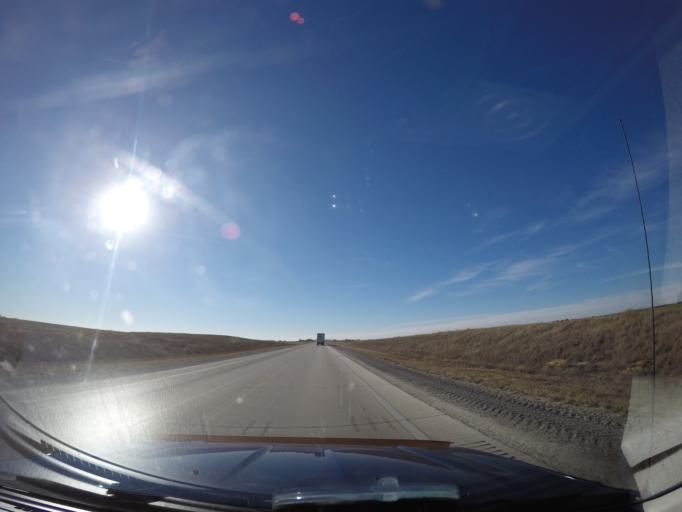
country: US
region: Kansas
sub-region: Marion County
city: Marion
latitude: 38.3577
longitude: -97.0821
